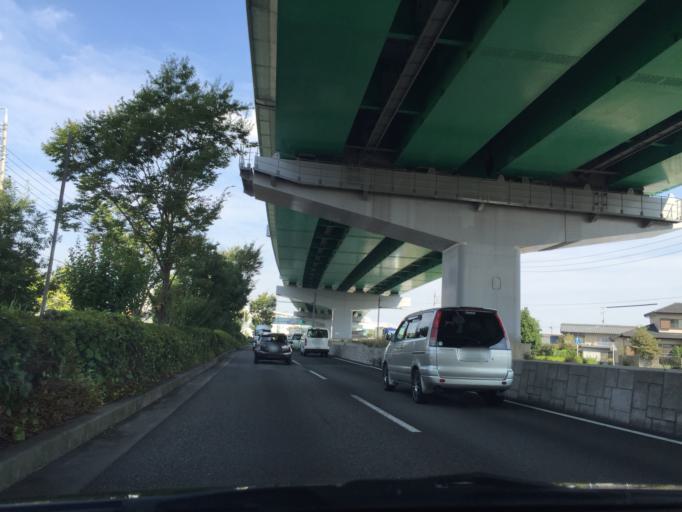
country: JP
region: Aichi
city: Ichinomiya
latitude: 35.3010
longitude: 136.7752
